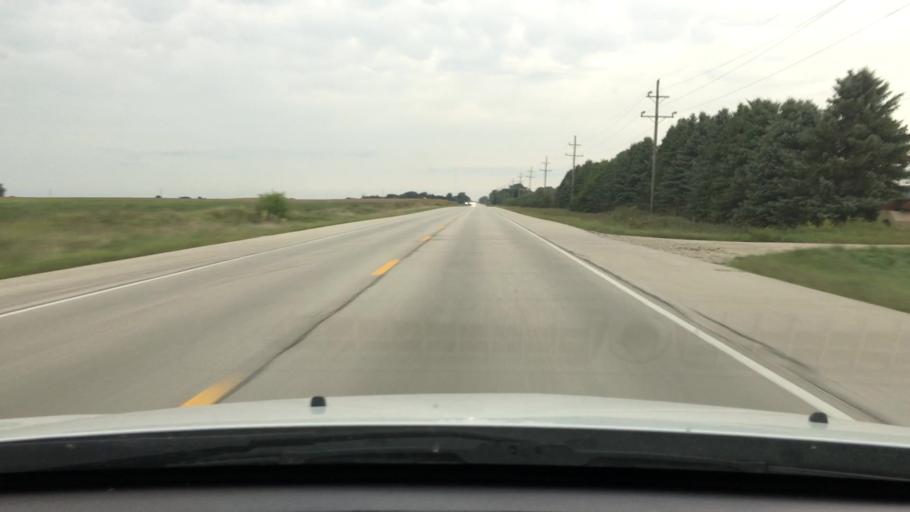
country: US
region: Illinois
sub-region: DeKalb County
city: Waterman
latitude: 41.8416
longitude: -88.7539
